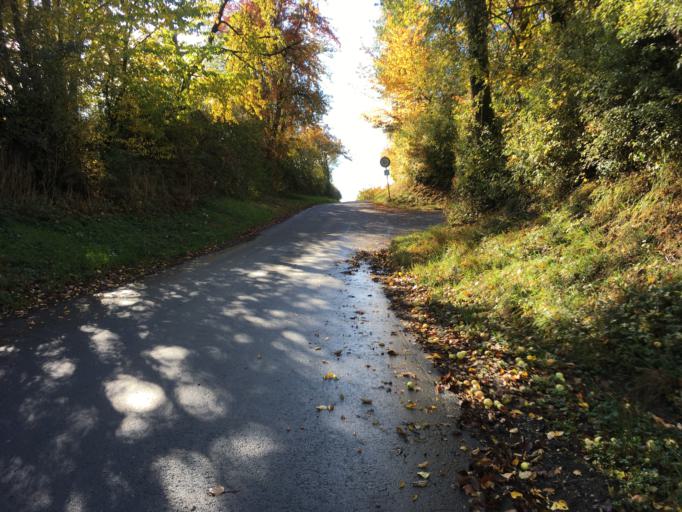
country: DE
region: Baden-Wuerttemberg
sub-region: Regierungsbezirk Stuttgart
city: Pfedelbach
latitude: 49.1879
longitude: 9.4803
